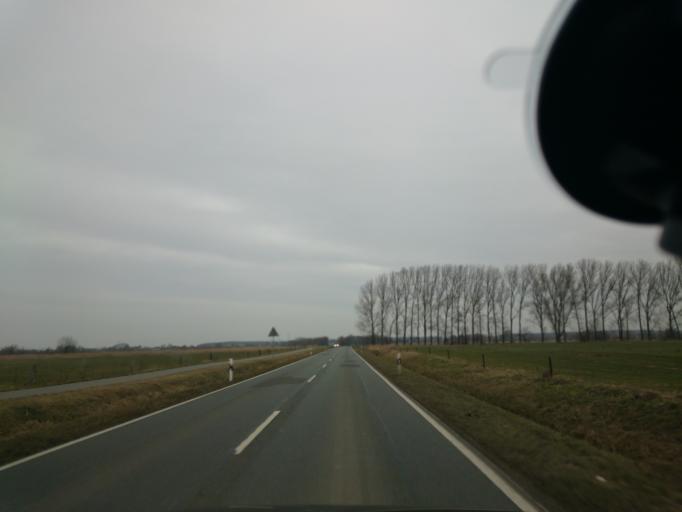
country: DE
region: Mecklenburg-Vorpommern
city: Borgerende-Rethwisch
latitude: 54.1279
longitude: 11.9260
